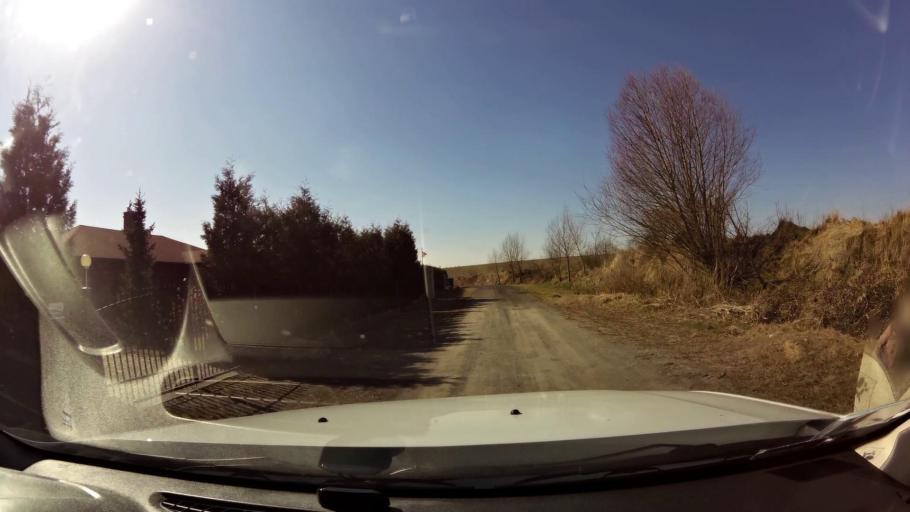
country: PL
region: West Pomeranian Voivodeship
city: Trzcinsko Zdroj
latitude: 52.9950
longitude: 14.6032
